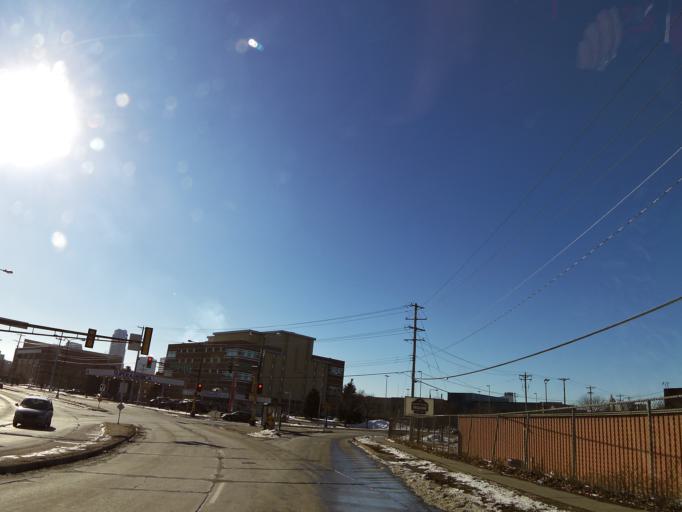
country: US
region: Minnesota
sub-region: Ramsey County
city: Saint Paul
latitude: 44.9583
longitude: -93.0845
